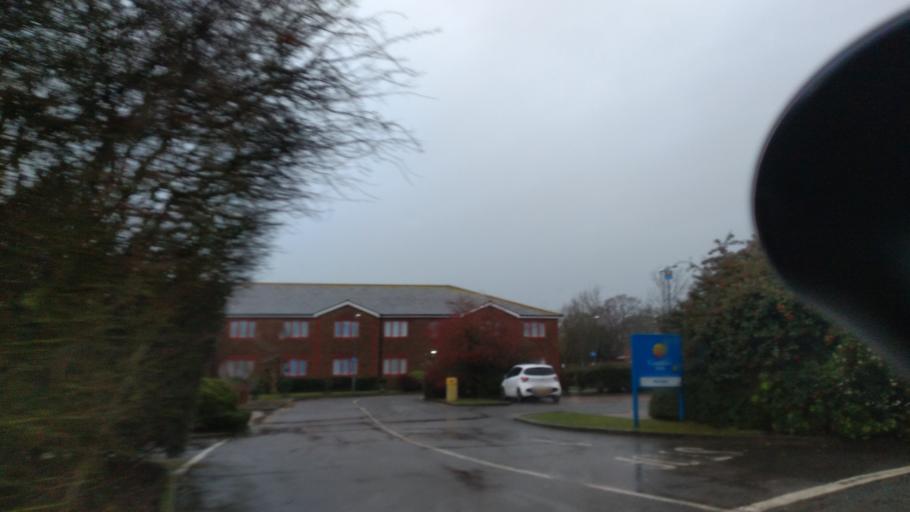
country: GB
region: England
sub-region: West Sussex
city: Arundel
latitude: 50.8427
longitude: -0.5423
